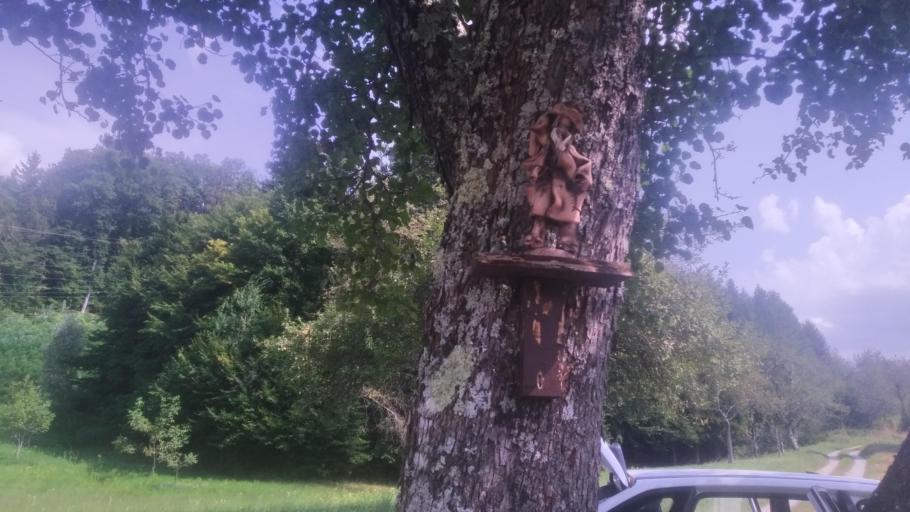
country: SI
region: Pivka
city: Pivka
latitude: 45.5968
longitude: 14.2060
